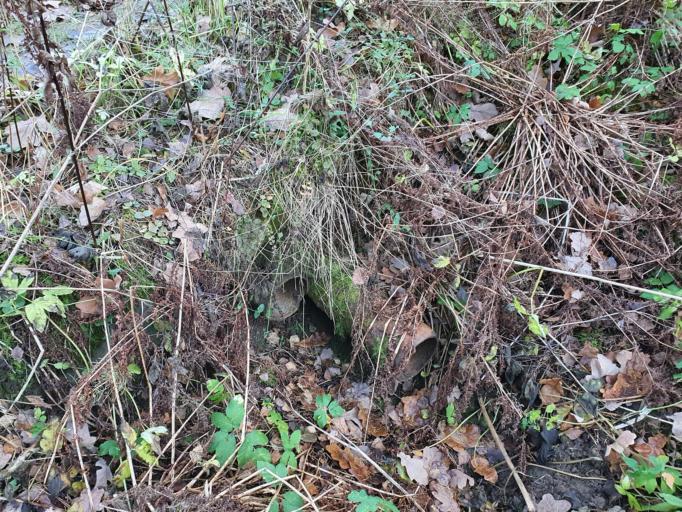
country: RU
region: St.-Petersburg
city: Tyarlevo
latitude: 59.6970
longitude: 30.4547
